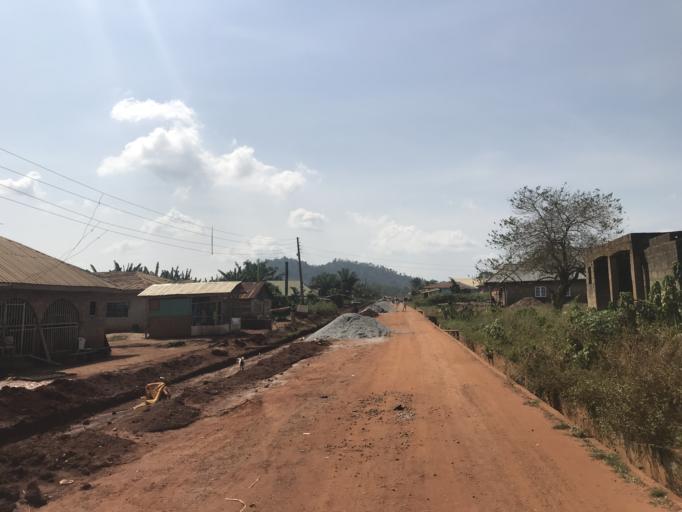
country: NG
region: Osun
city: Ilesa
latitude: 7.6216
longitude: 4.7044
